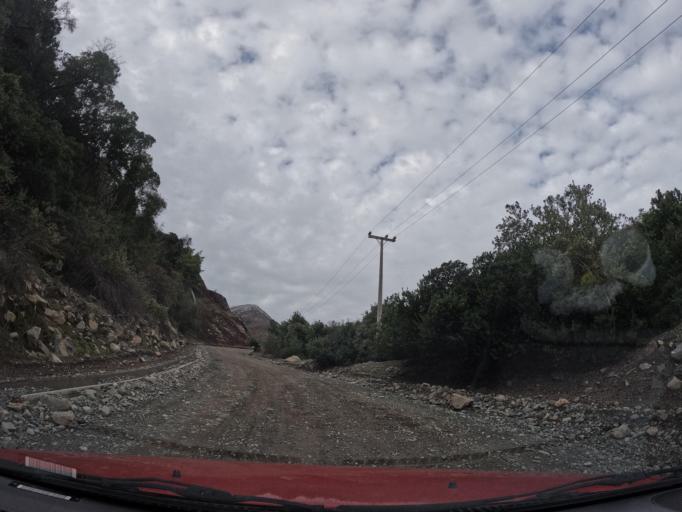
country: CL
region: Maule
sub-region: Provincia de Linares
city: Colbun
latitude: -35.8576
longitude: -71.2088
